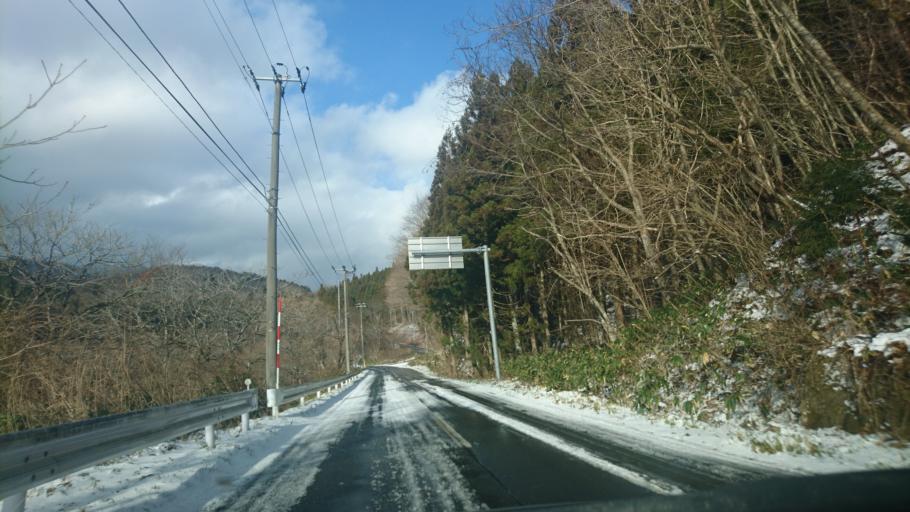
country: JP
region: Iwate
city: Tono
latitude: 39.1659
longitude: 141.3659
